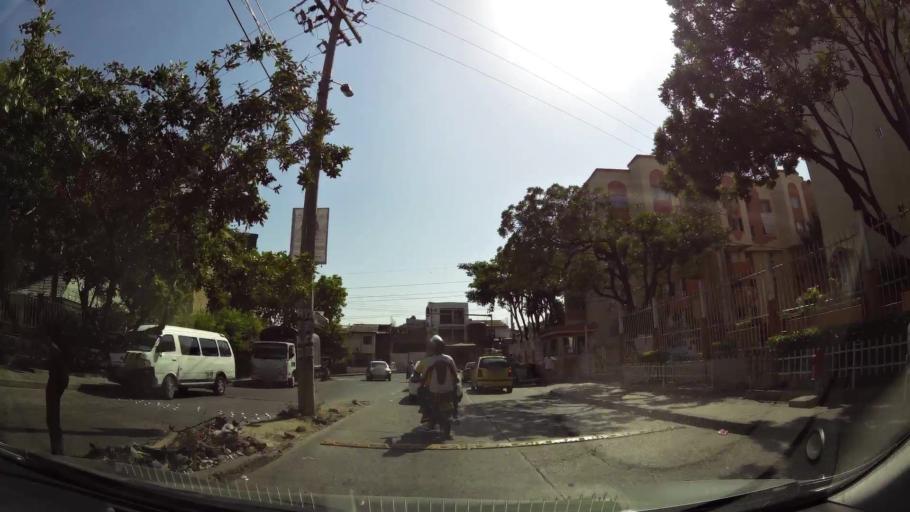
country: CO
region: Bolivar
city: Cartagena
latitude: 10.3966
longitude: -75.4943
